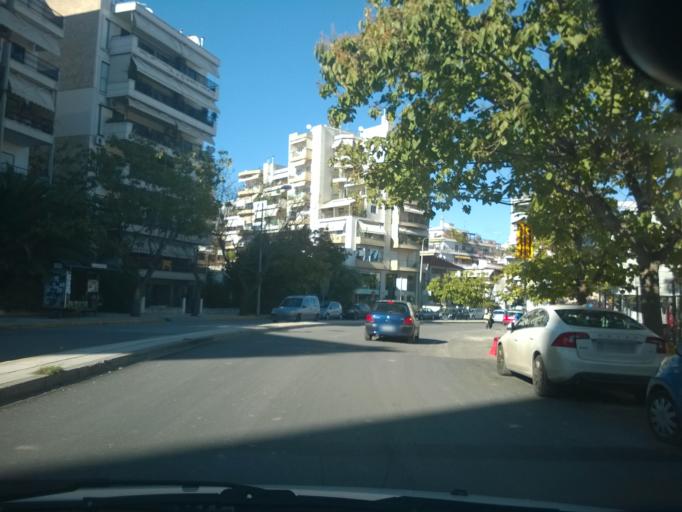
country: GR
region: Central Macedonia
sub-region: Nomos Thessalonikis
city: Kalamaria
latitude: 40.5952
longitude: 22.9598
